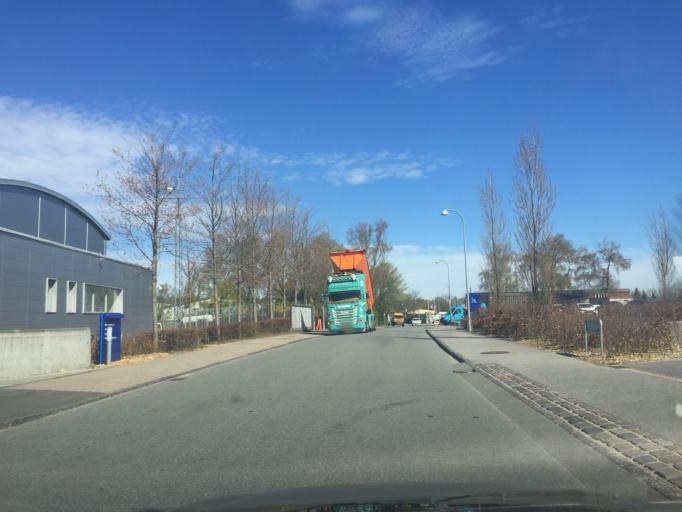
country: DK
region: Capital Region
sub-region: Herlev Kommune
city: Herlev
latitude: 55.7551
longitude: 12.4475
